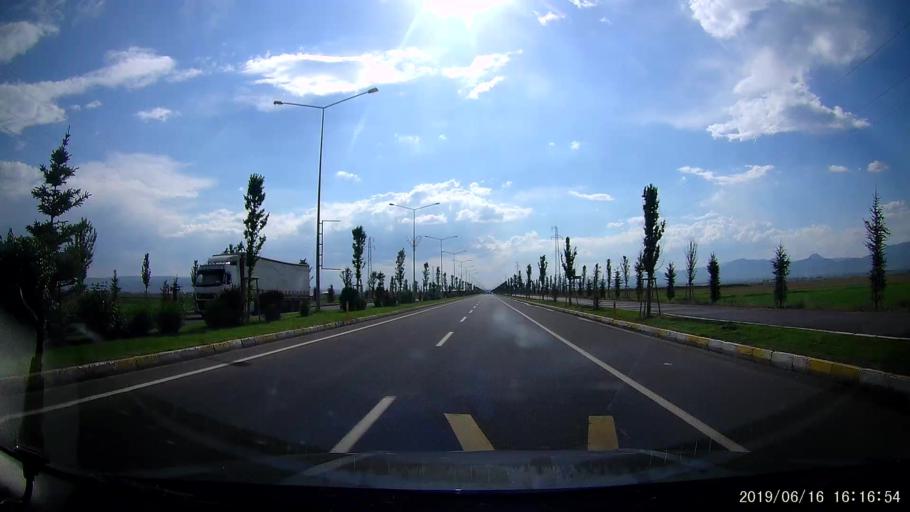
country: TR
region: Erzurum
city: Ilica
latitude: 39.9633
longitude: 41.1984
